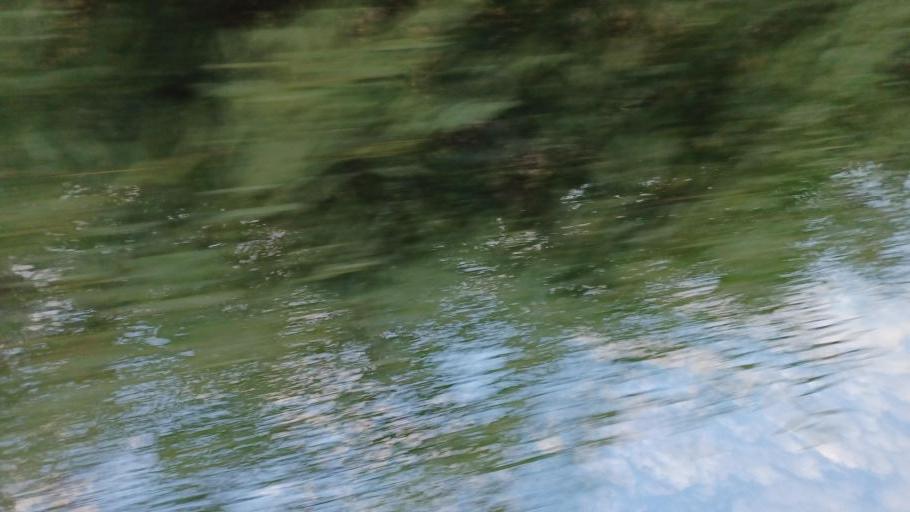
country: CY
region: Limassol
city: Pelendri
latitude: 34.8367
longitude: 32.9567
